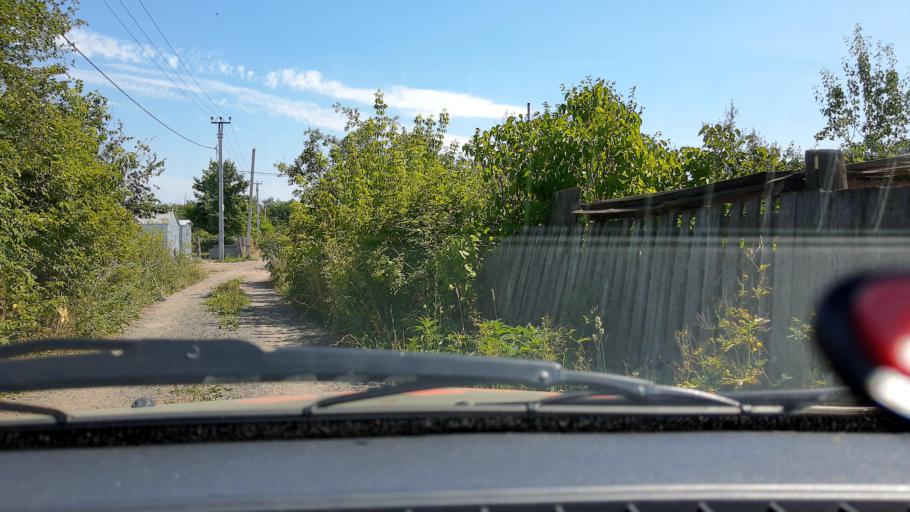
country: RU
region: Bashkortostan
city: Mikhaylovka
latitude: 54.7959
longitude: 55.8345
